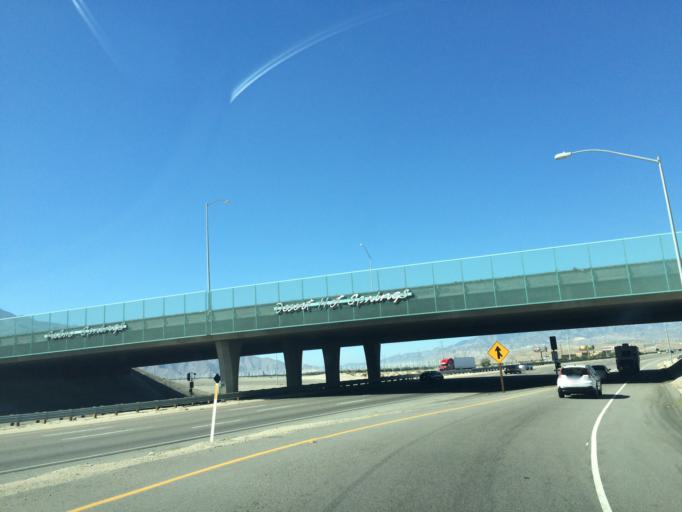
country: US
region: California
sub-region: Riverside County
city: Garnet
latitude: 33.8794
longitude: -116.5028
